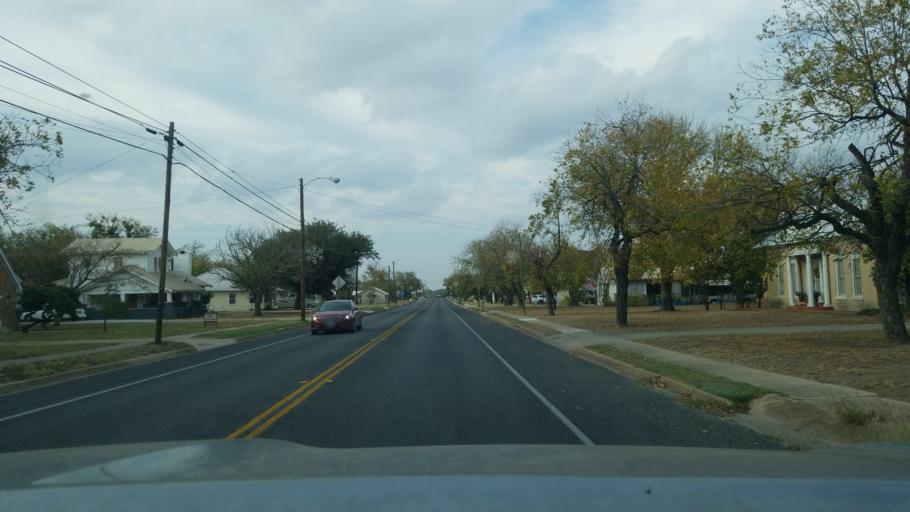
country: US
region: Texas
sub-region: Mills County
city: Goldthwaite
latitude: 31.4569
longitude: -98.5720
